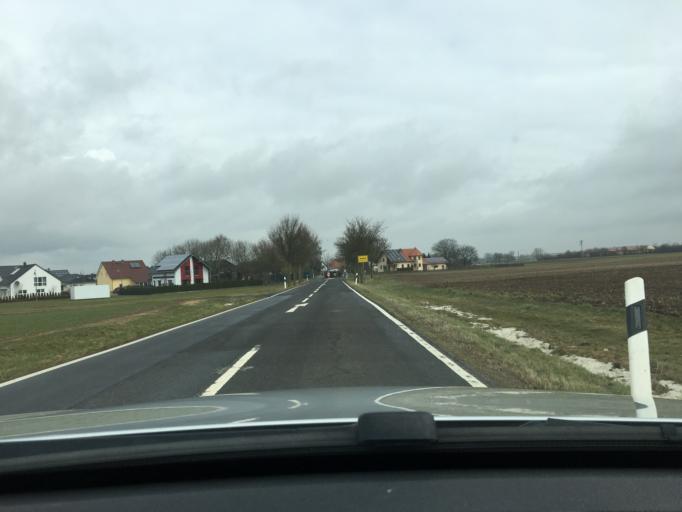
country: DE
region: Rheinland-Pfalz
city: Ilbesheim
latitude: 49.6847
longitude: 8.0762
